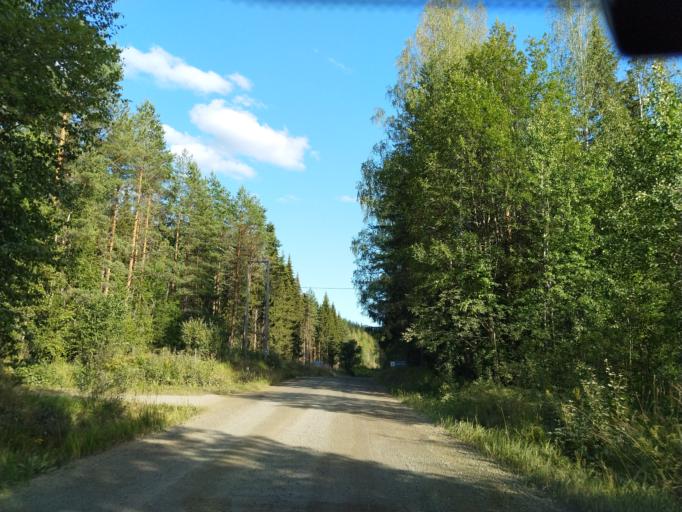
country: FI
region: Central Finland
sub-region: Jaemsae
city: Kuhmoinen
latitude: 61.7080
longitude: 24.9136
